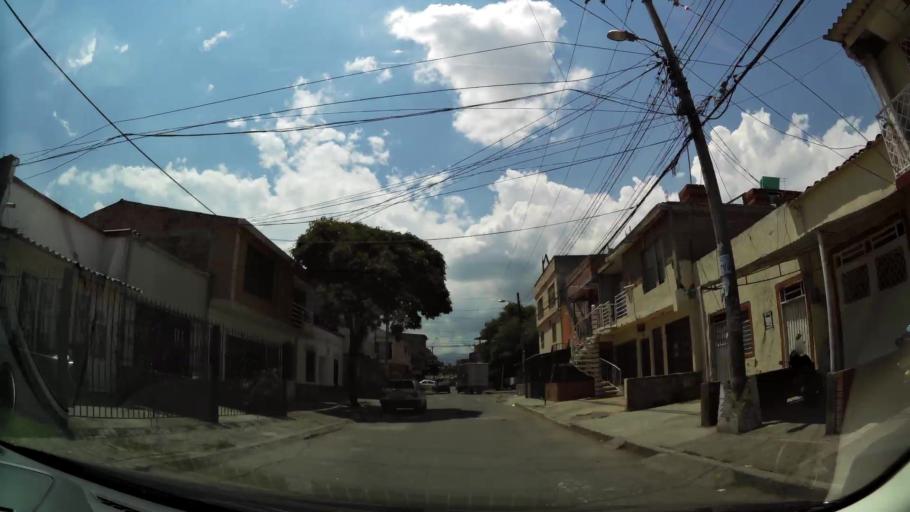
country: CO
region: Valle del Cauca
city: Cali
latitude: 3.4479
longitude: -76.5017
